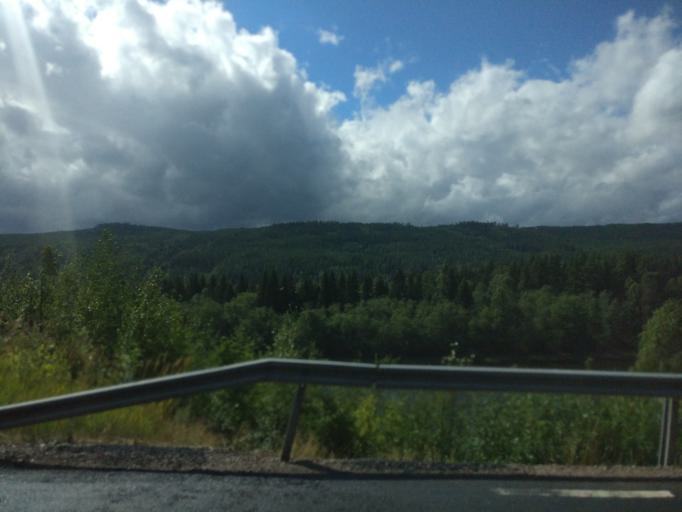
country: SE
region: Vaermland
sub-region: Hagfors Kommun
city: Ekshaerad
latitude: 60.3439
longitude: 13.3492
